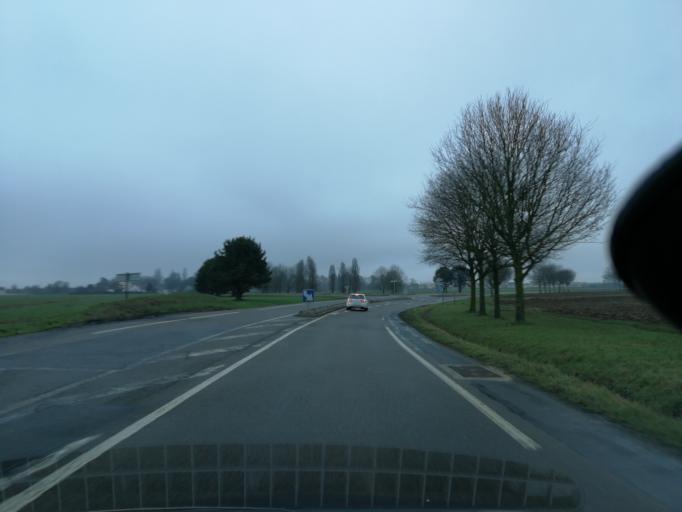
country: FR
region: Ile-de-France
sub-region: Departement de l'Essonne
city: Villiers-le-Bacle
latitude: 48.7394
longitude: 2.1091
